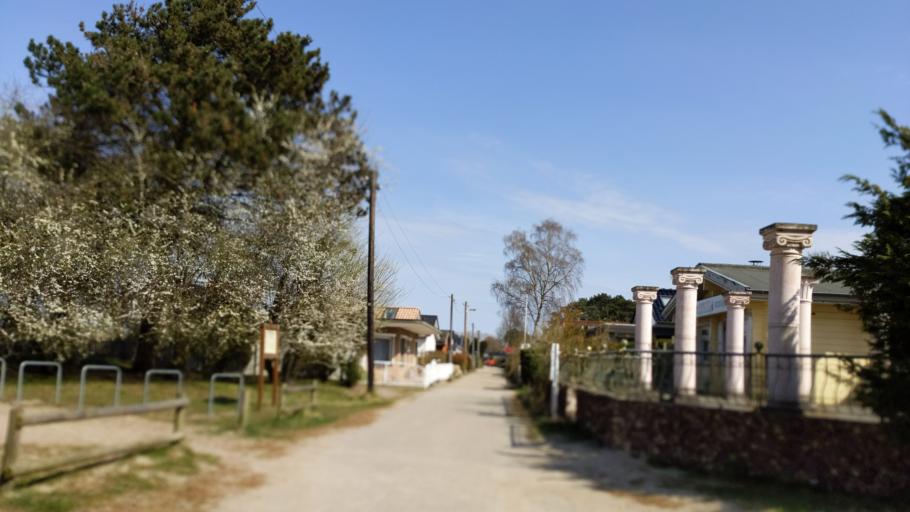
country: DE
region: Schleswig-Holstein
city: Travemuende
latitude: 53.9553
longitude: 10.8956
